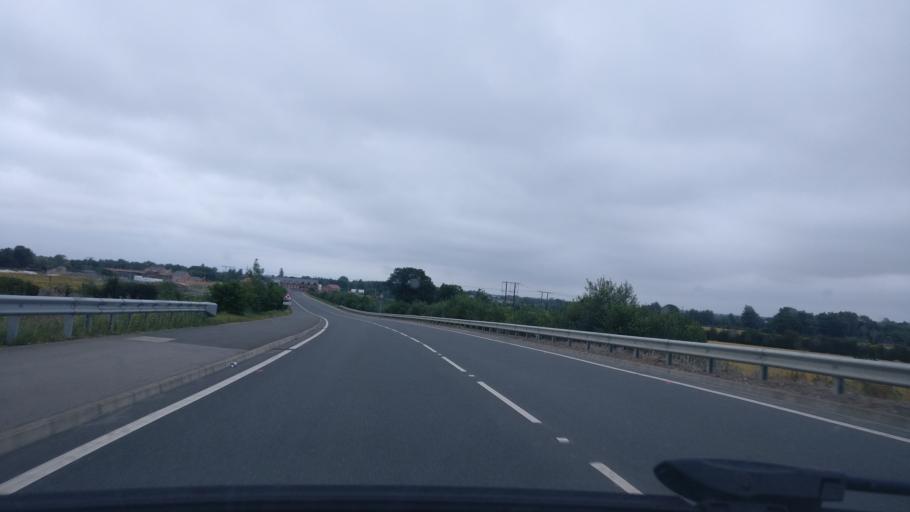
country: GB
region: England
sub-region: East Riding of Yorkshire
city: Beverley
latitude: 53.8283
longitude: -0.4169
